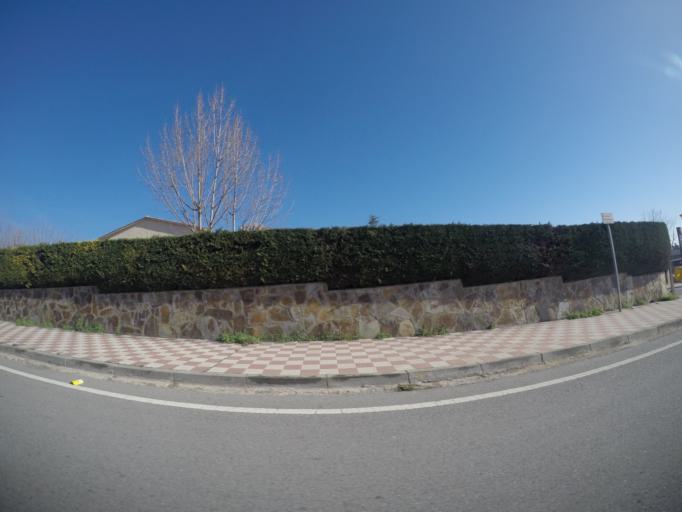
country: ES
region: Catalonia
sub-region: Provincia de Barcelona
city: Collbato
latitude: 41.5633
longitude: 1.8147
